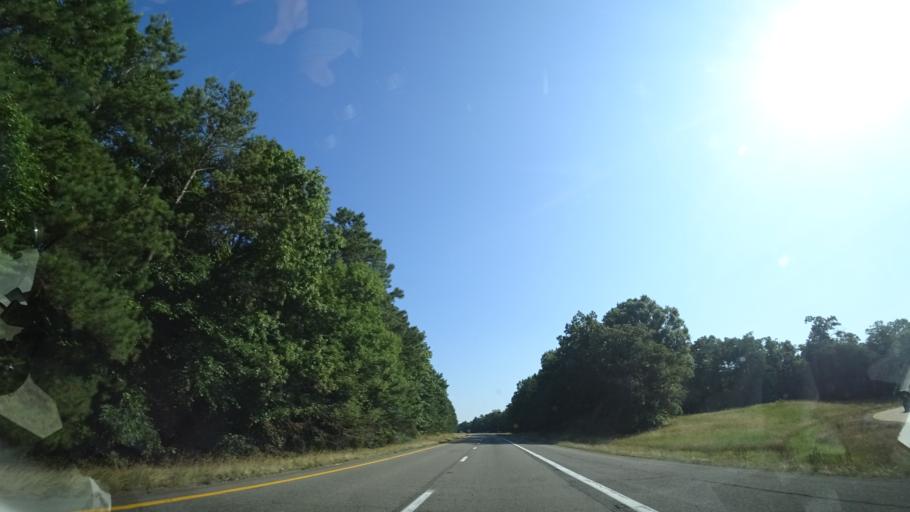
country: US
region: Virginia
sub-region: Henrico County
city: Sandston
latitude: 37.5106
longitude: -77.2728
